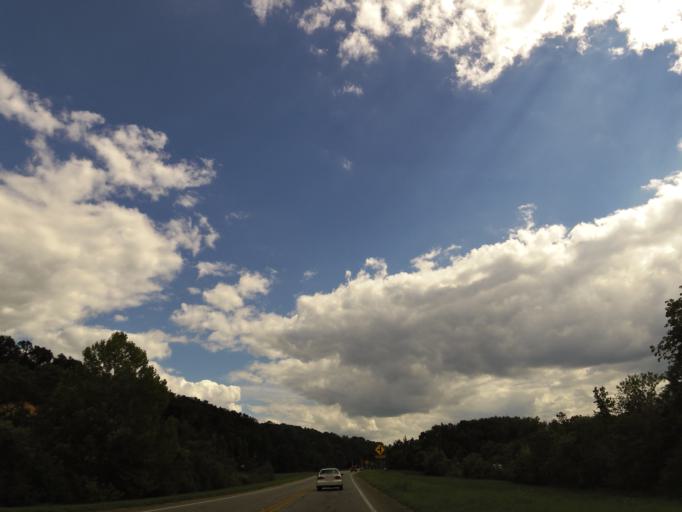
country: US
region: Georgia
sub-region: Walker County
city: Chattanooga Valley
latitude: 34.9532
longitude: -85.3331
